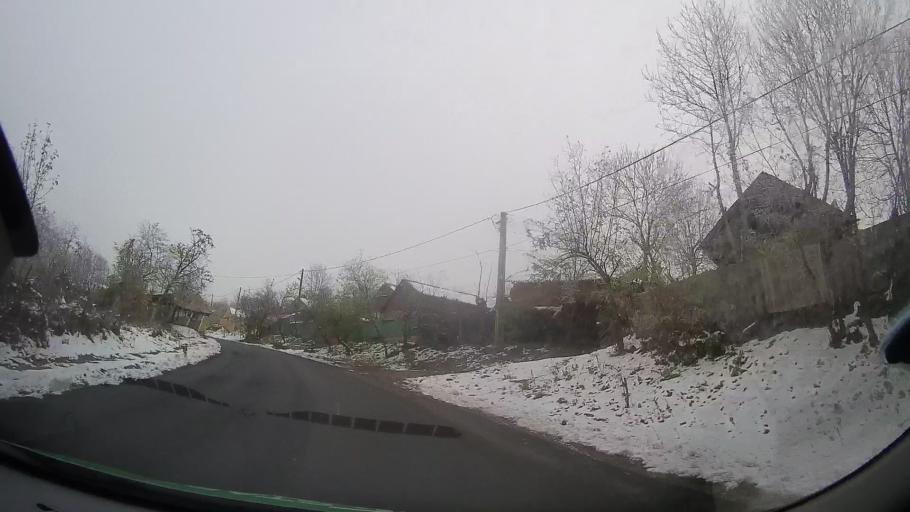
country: RO
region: Vaslui
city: Coroiesti
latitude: 46.2105
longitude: 27.4417
